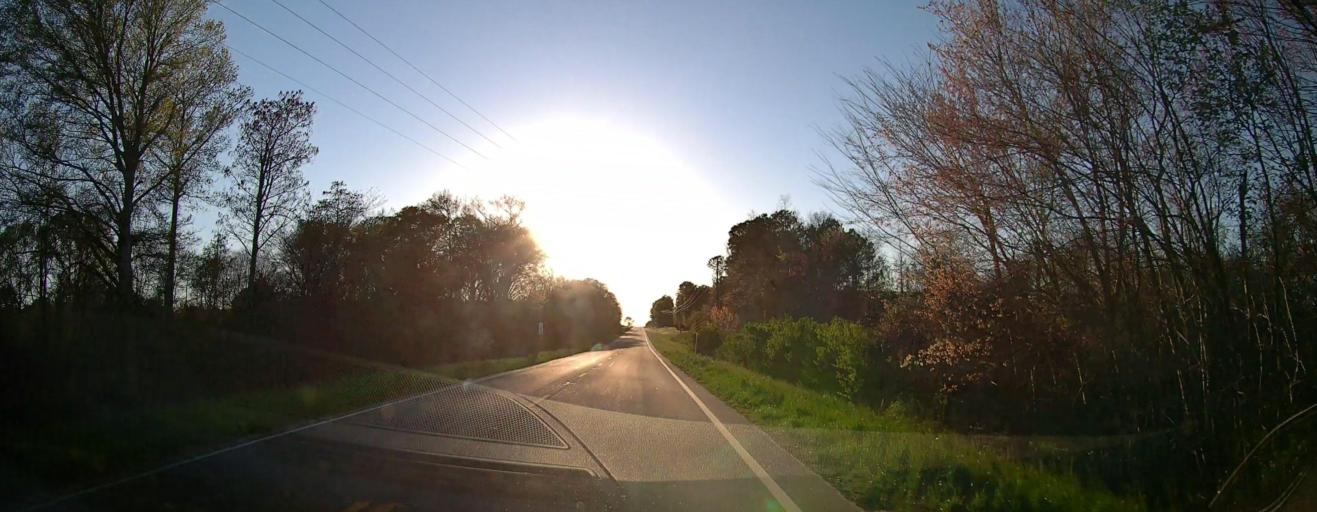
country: US
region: Georgia
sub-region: Wilcox County
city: Rochelle
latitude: 31.9500
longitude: -83.4796
